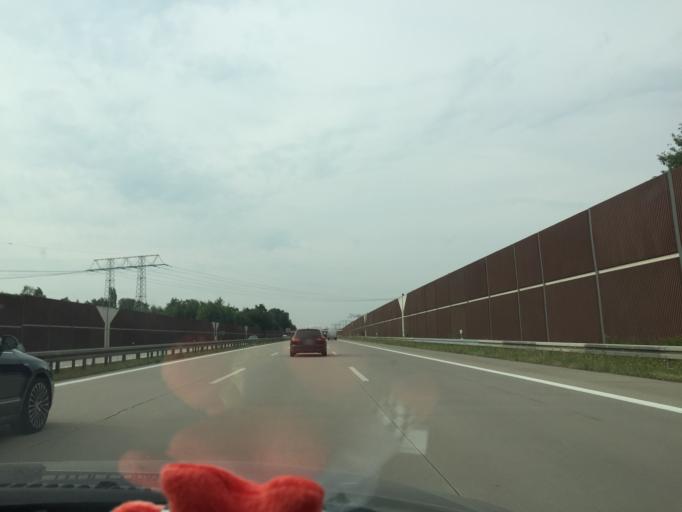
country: DE
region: Brandenburg
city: Neuenhagen
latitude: 52.5120
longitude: 13.7314
